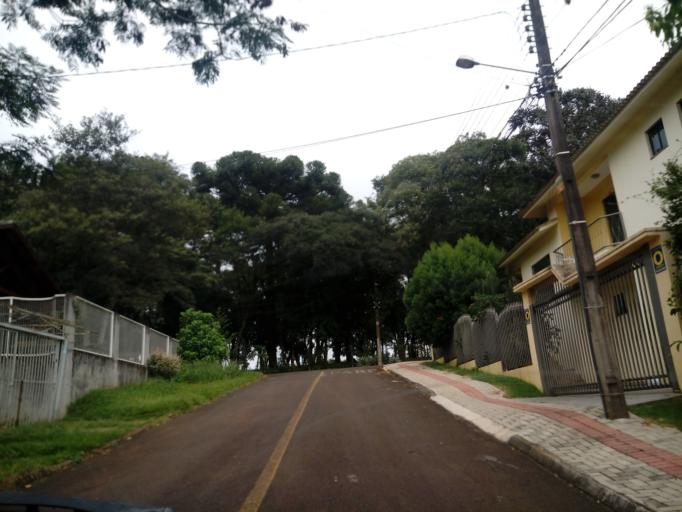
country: BR
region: Santa Catarina
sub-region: Chapeco
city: Chapeco
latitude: -27.0983
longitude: -52.6413
